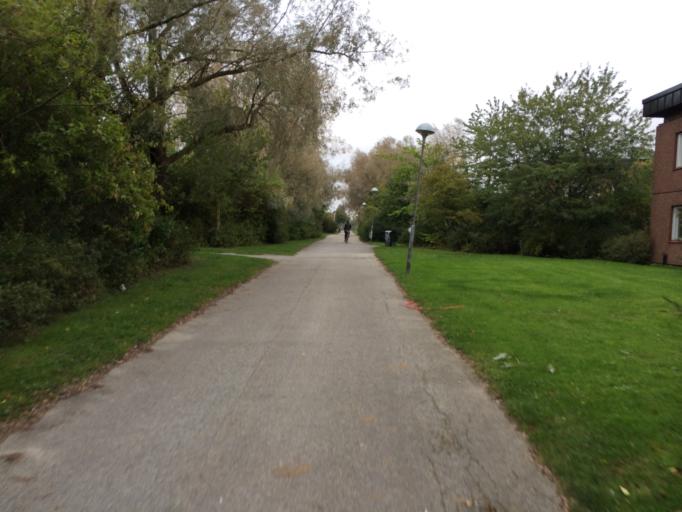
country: SE
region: Skane
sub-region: Lunds Kommun
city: Lund
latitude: 55.7094
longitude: 13.2344
